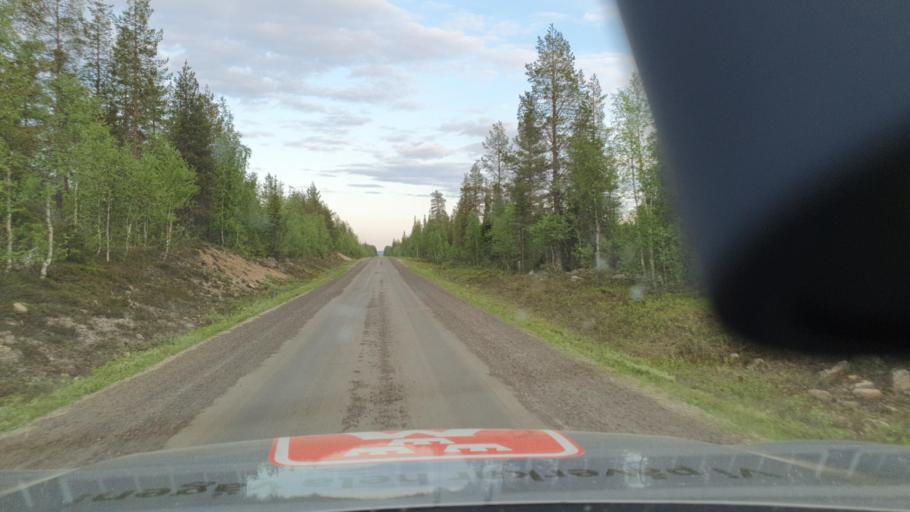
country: SE
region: Norrbotten
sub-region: Gallivare Kommun
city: Gaellivare
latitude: 66.6320
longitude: 21.3297
